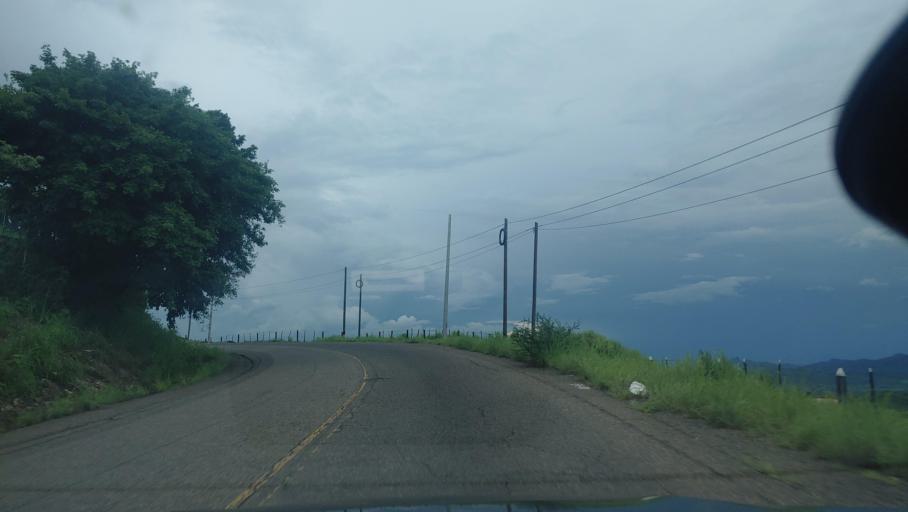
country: HN
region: Choluteca
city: Corpus
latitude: 13.3717
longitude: -87.0584
